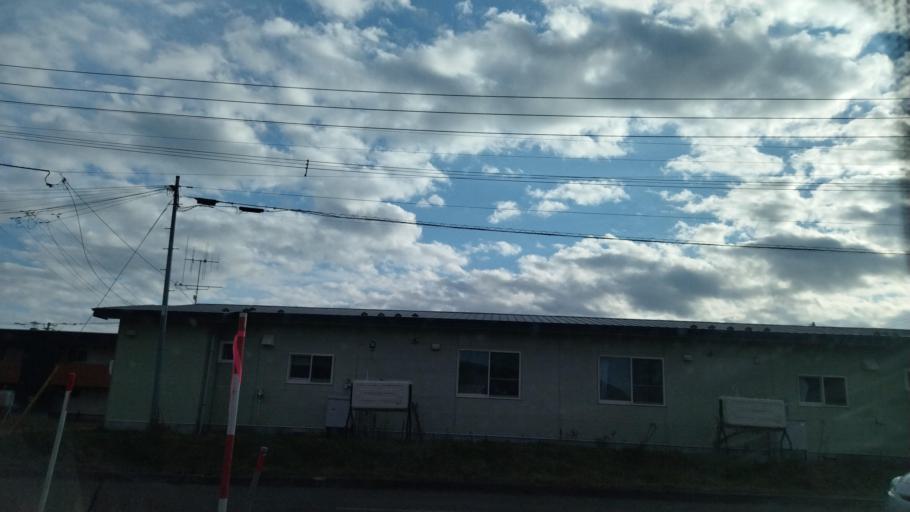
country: JP
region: Hokkaido
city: Otofuke
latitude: 43.2468
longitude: 143.5505
